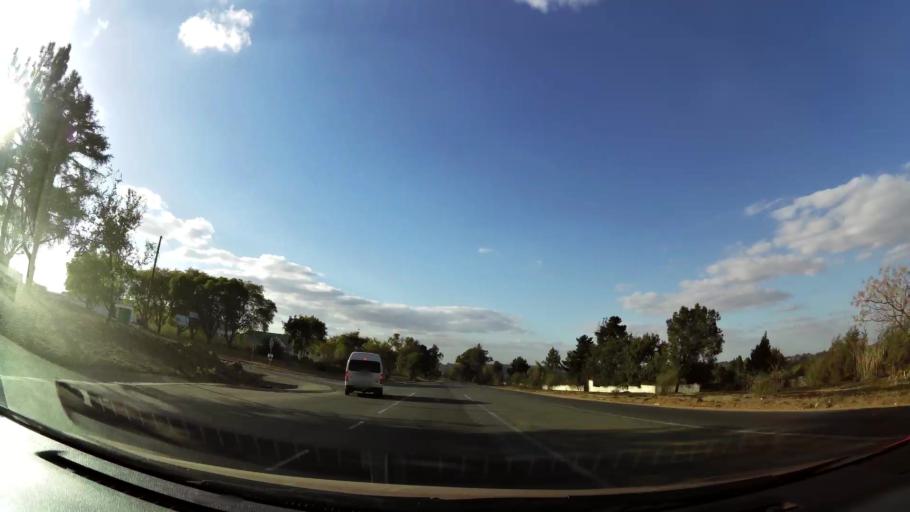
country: ZA
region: Gauteng
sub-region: City of Johannesburg Metropolitan Municipality
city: Midrand
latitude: -25.9721
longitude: 28.1359
